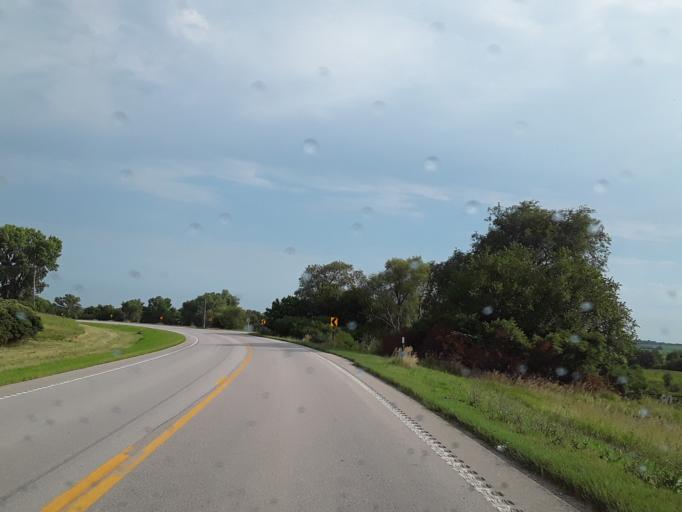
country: US
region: Nebraska
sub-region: Saunders County
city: Ashland
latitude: 41.0928
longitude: -96.4260
